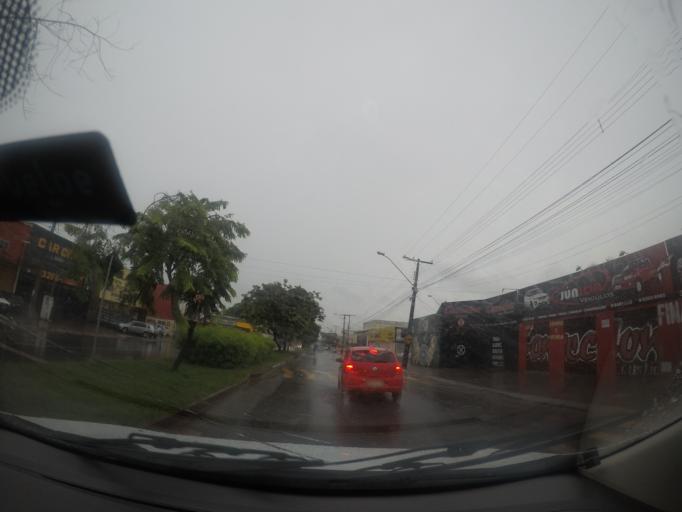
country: BR
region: Goias
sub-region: Goiania
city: Goiania
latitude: -16.6274
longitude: -49.3318
